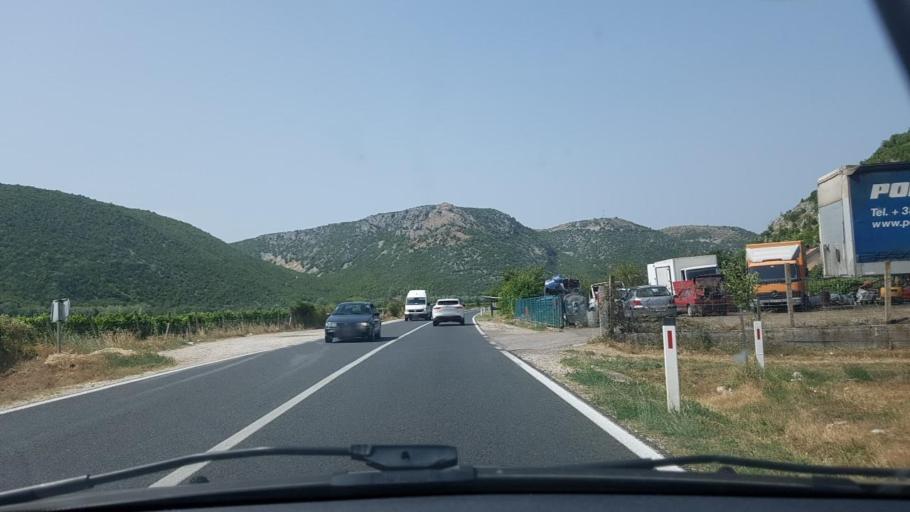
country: BA
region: Federation of Bosnia and Herzegovina
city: Citluk
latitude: 43.1865
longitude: 17.7811
